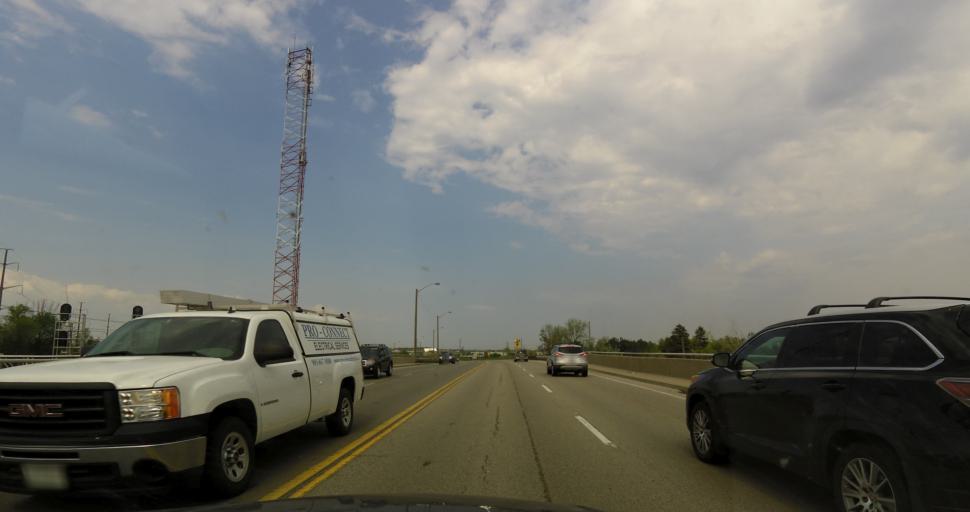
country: CA
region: Ontario
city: Oakville
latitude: 43.4871
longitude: -79.6563
